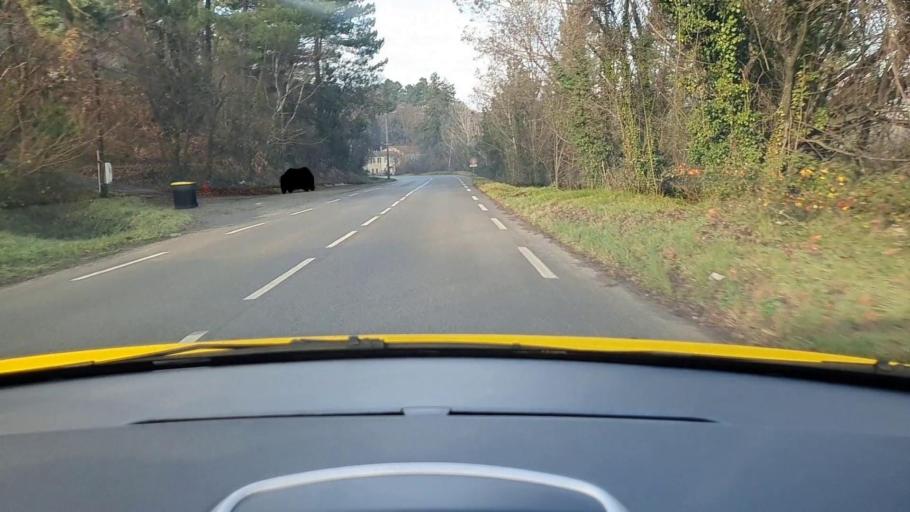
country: FR
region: Languedoc-Roussillon
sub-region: Departement du Gard
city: Branoux-les-Taillades
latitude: 44.2773
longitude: 4.0066
